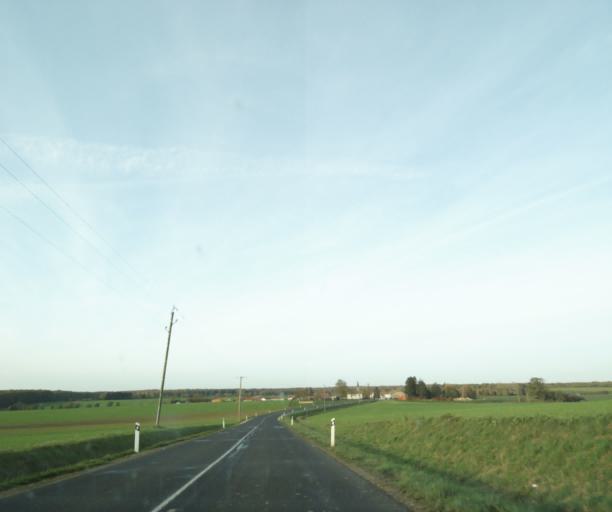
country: FR
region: Lorraine
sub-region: Departement de la Meuse
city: Etain
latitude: 49.1490
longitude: 5.6266
